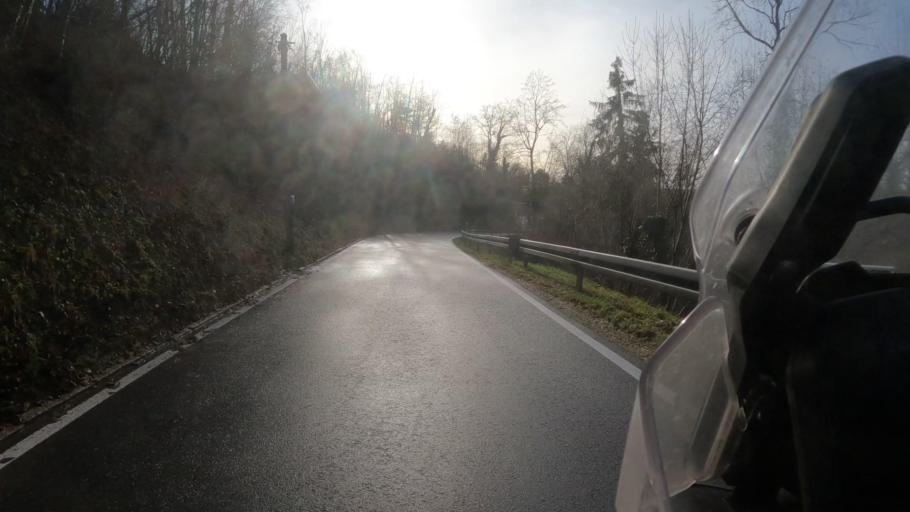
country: DE
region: Baden-Wuerttemberg
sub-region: Freiburg Region
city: Tengen
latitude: 47.8121
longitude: 8.6602
